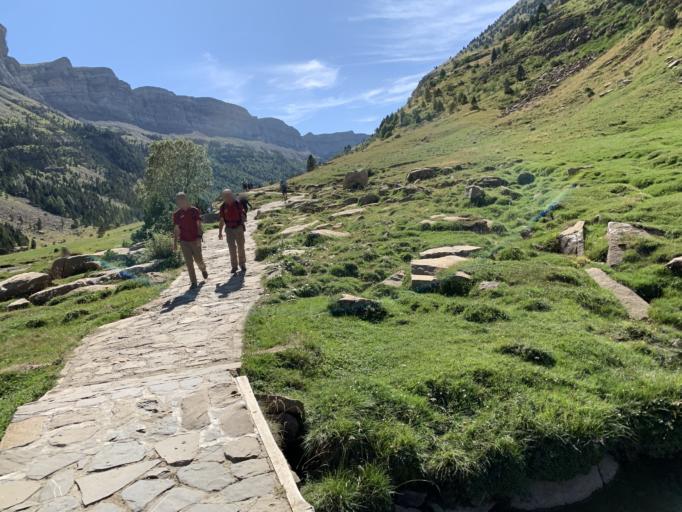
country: ES
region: Aragon
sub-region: Provincia de Huesca
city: Broto
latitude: 42.6410
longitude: 0.0054
